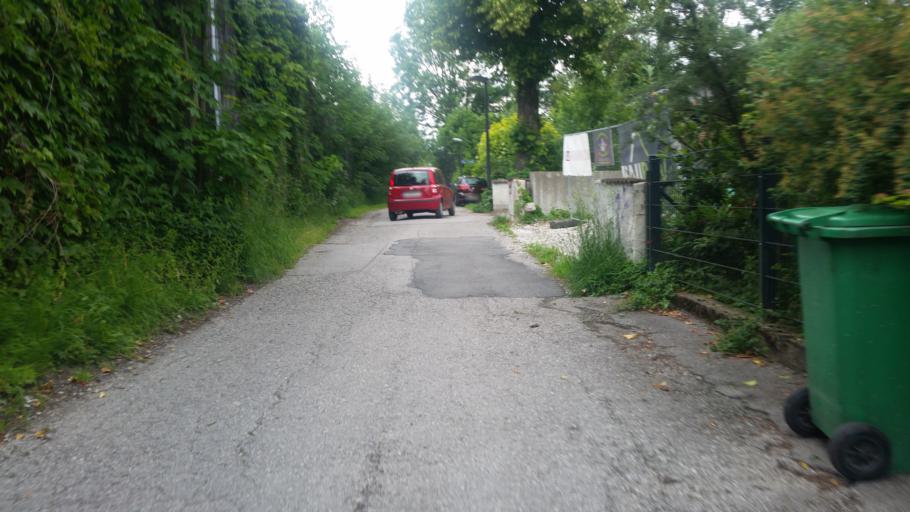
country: AT
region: Salzburg
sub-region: Salzburg Stadt
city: Salzburg
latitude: 47.7970
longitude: 13.0739
